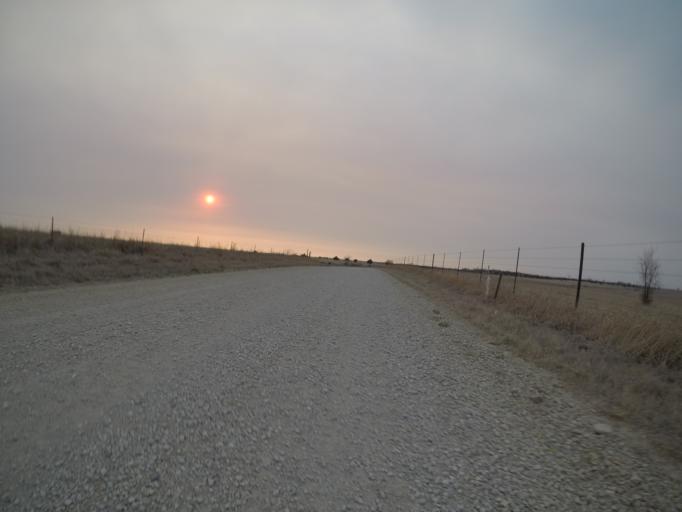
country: US
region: Kansas
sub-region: Riley County
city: Manhattan
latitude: 39.2325
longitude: -96.6486
